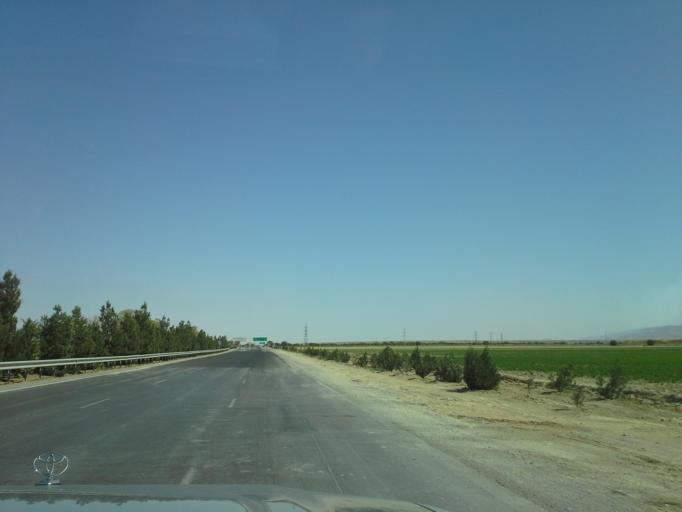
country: TM
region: Ahal
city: Annau
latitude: 37.9056
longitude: 58.5332
